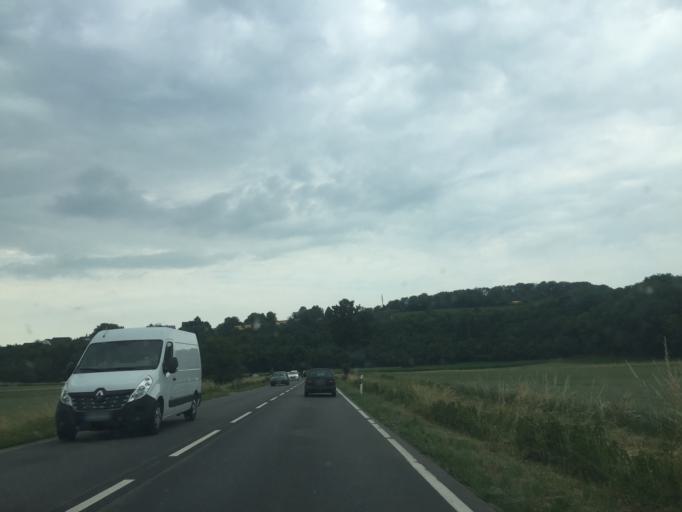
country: DE
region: Baden-Wuerttemberg
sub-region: Karlsruhe Region
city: Sinsheim
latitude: 49.2622
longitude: 8.8495
